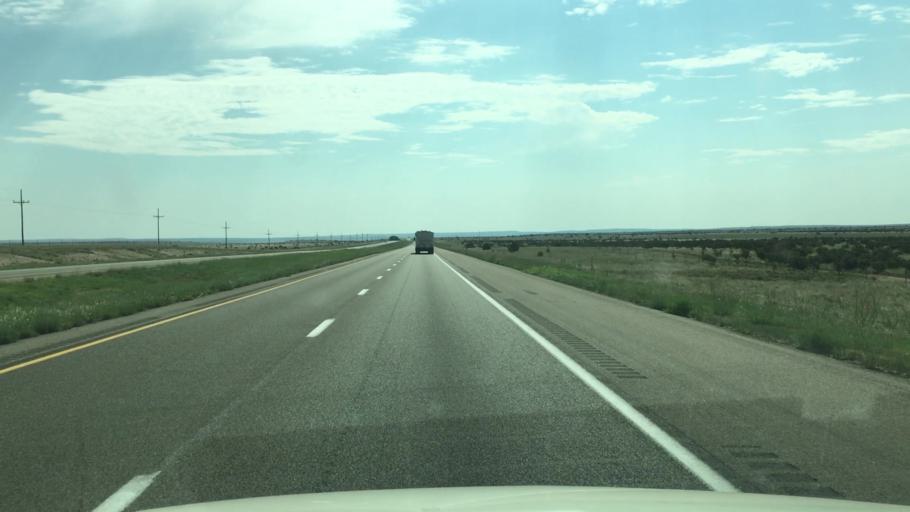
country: US
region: New Mexico
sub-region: Guadalupe County
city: Santa Rosa
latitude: 34.9829
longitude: -105.1230
